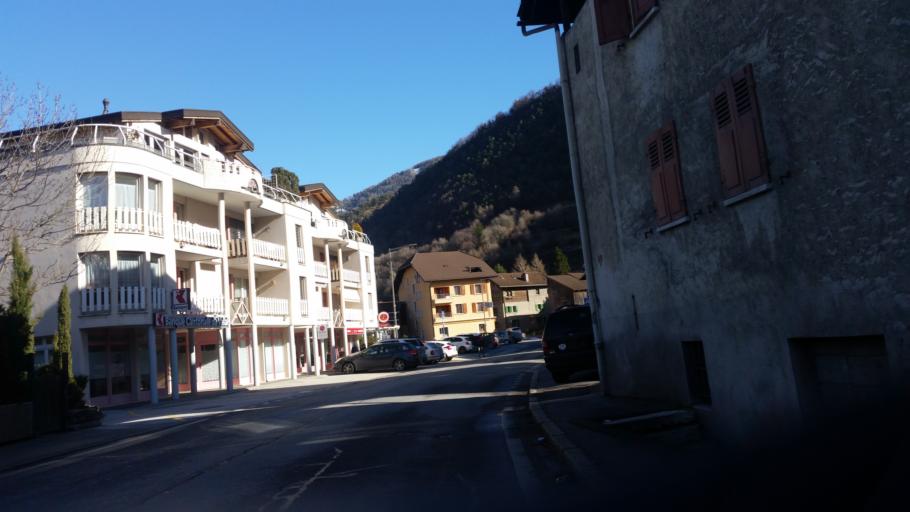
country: CH
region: Valais
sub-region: Sierre District
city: Grone
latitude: 46.2511
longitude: 7.4571
